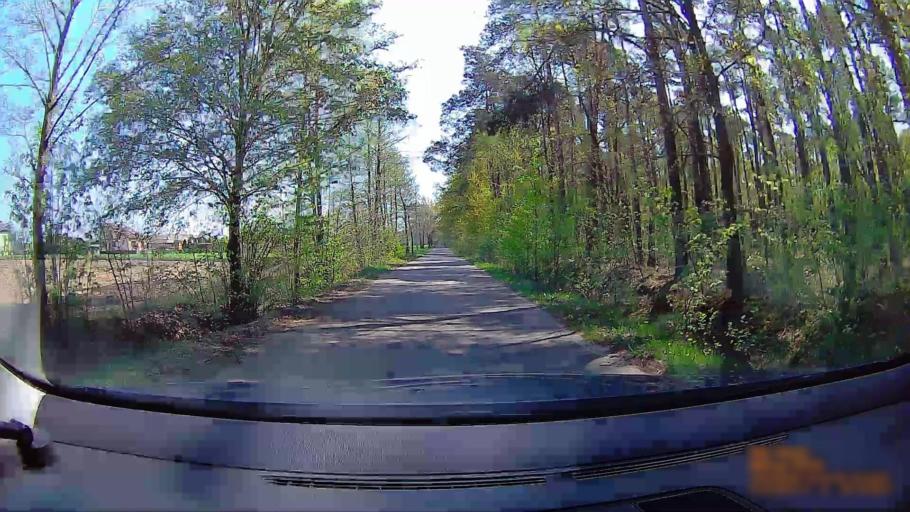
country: PL
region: Greater Poland Voivodeship
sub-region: Powiat koninski
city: Rychwal
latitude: 52.0937
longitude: 18.1720
